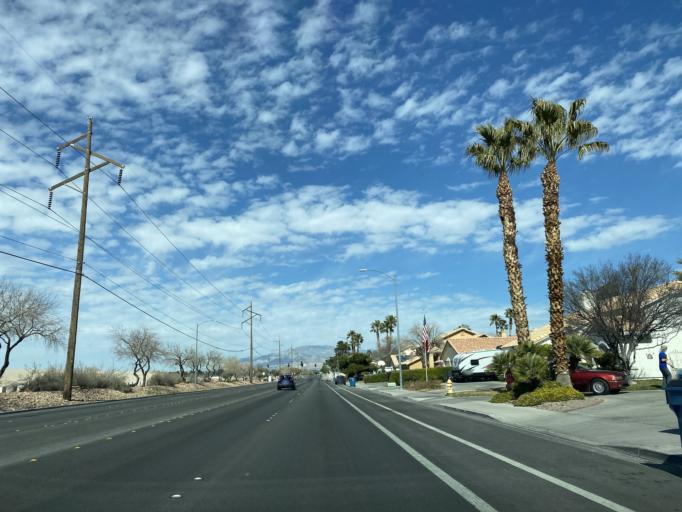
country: US
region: Nevada
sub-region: Clark County
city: Spring Valley
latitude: 36.2236
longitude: -115.2514
